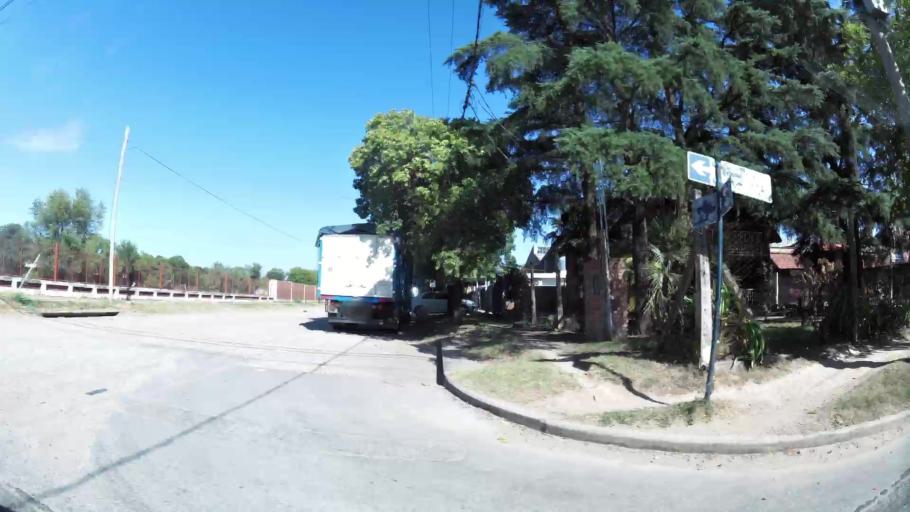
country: AR
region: Cordoba
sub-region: Departamento de Capital
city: Cordoba
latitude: -31.4635
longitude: -64.1869
